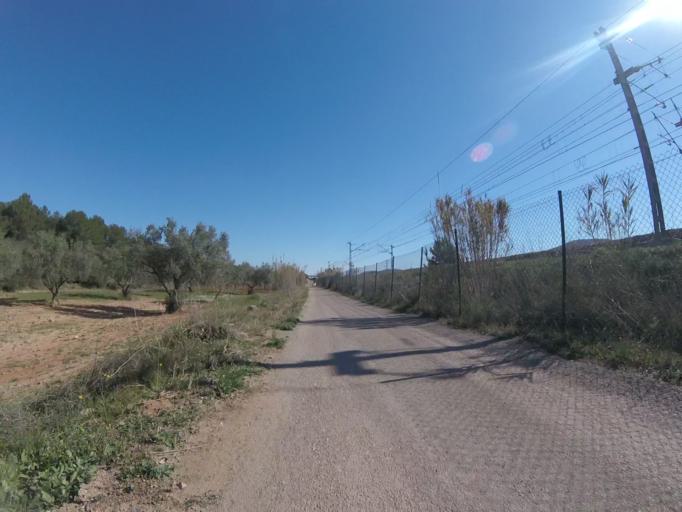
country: ES
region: Valencia
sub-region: Provincia de Castello
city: Santa Magdalena de Pulpis
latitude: 40.3449
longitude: 0.2693
